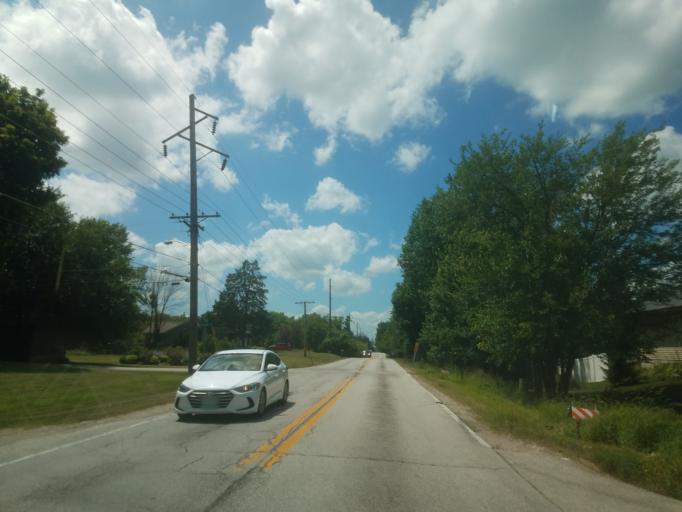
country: US
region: Illinois
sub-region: McLean County
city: Bloomington
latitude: 40.4590
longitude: -89.0108
